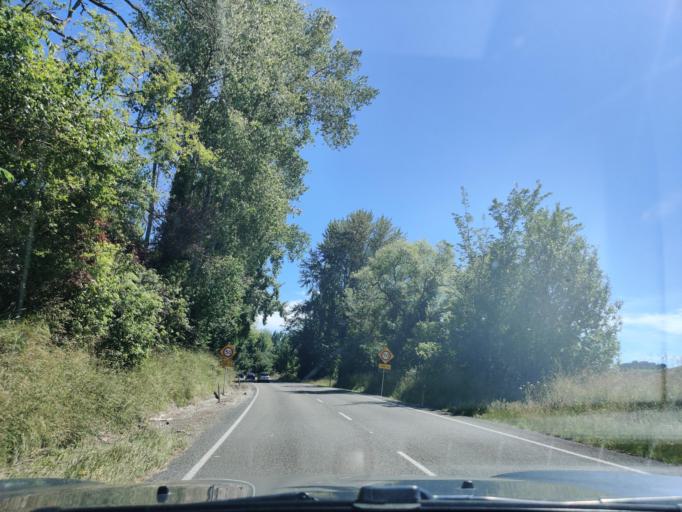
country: NZ
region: Manawatu-Wanganui
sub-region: Rangitikei District
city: Bulls
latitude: -39.9439
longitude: 175.5692
